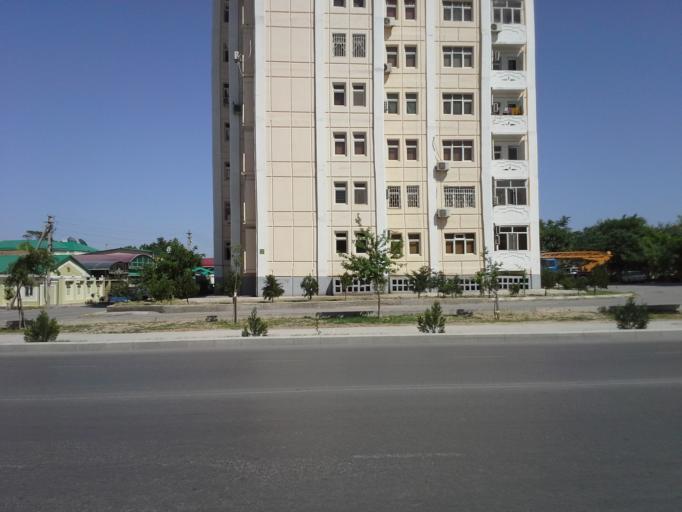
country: TM
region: Ahal
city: Ashgabat
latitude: 37.9535
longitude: 58.3558
